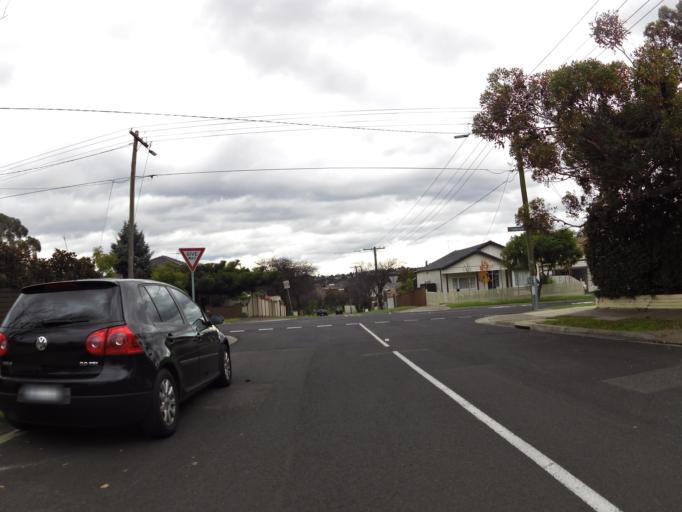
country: AU
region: Victoria
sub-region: Moonee Valley
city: Moonee Ponds
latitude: -37.7540
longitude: 144.9283
